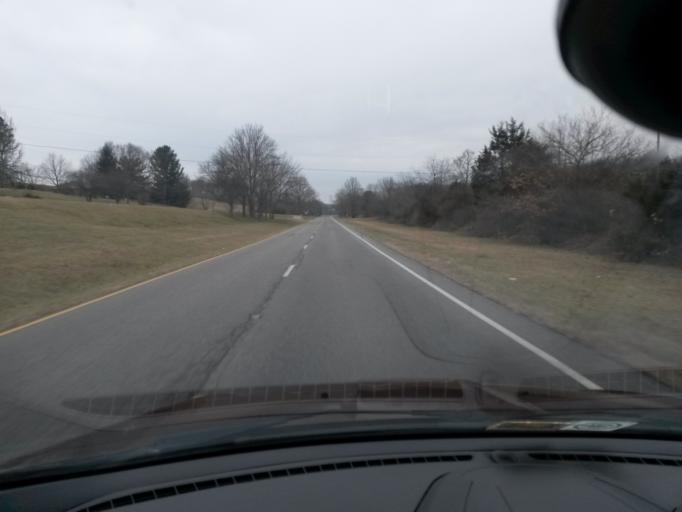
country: US
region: Virginia
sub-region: Augusta County
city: Stuarts Draft
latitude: 37.9385
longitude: -79.1903
